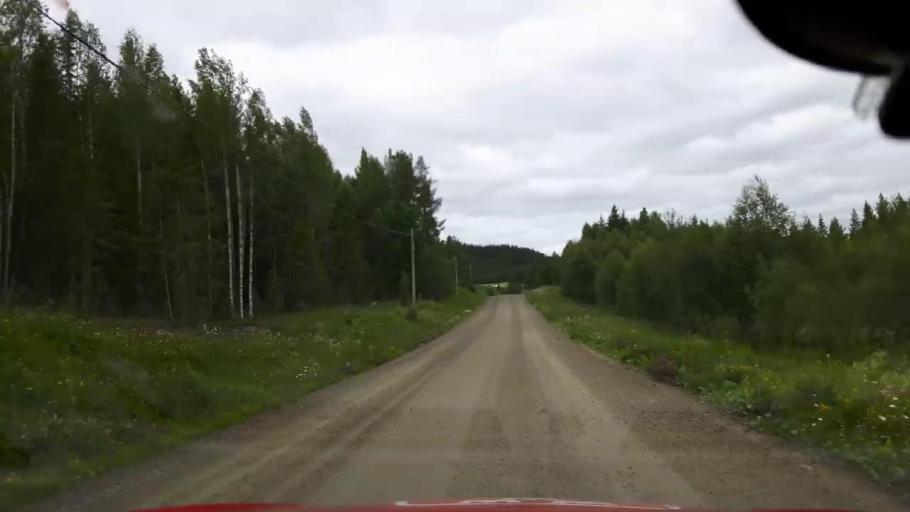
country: SE
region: Jaemtland
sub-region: OEstersunds Kommun
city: Brunflo
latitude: 62.9055
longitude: 15.1013
